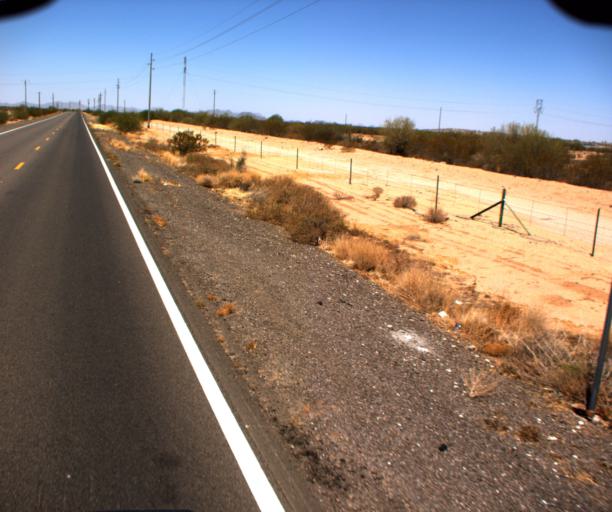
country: US
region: Arizona
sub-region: Pinal County
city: Maricopa
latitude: 33.0726
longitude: -112.1977
